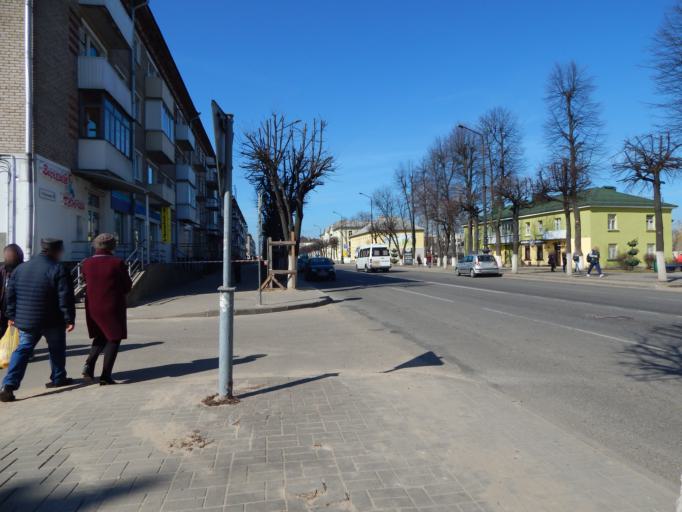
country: BY
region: Minsk
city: Horad Barysaw
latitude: 54.2228
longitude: 28.5180
